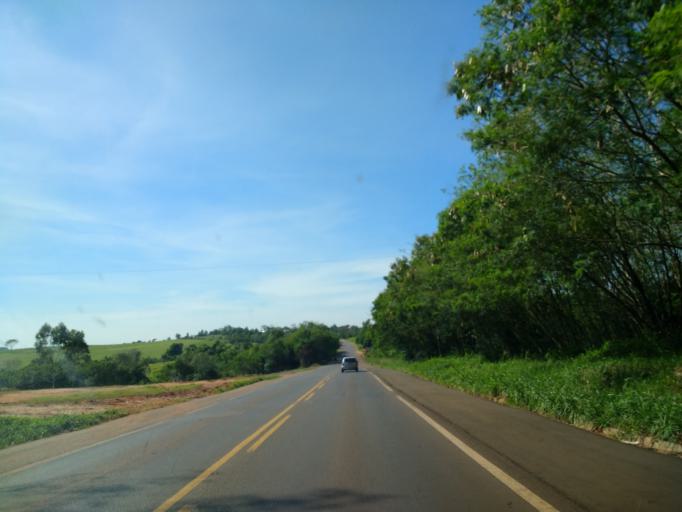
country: BR
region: Parana
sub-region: Alto Piquiri
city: Alto Piquiri
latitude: -23.8913
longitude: -53.4182
